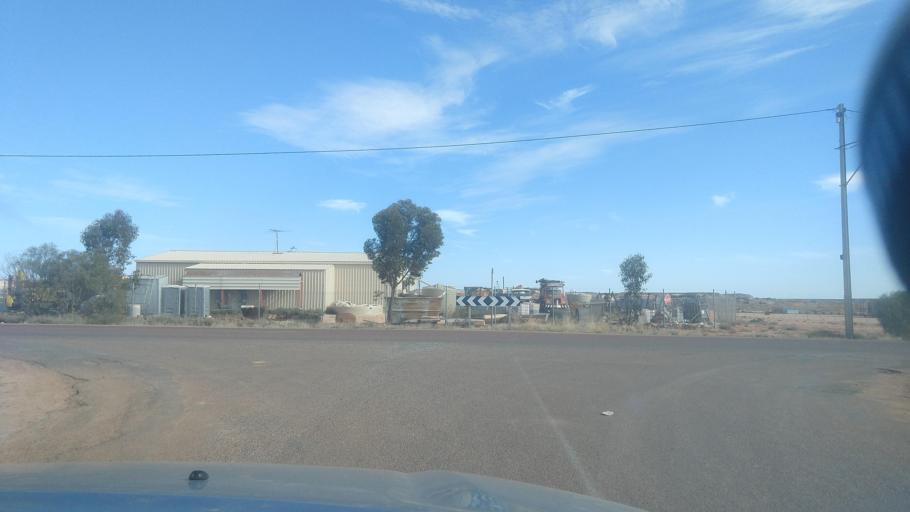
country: AU
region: South Australia
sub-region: Coober Pedy
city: Coober Pedy
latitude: -29.0140
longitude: 134.7460
